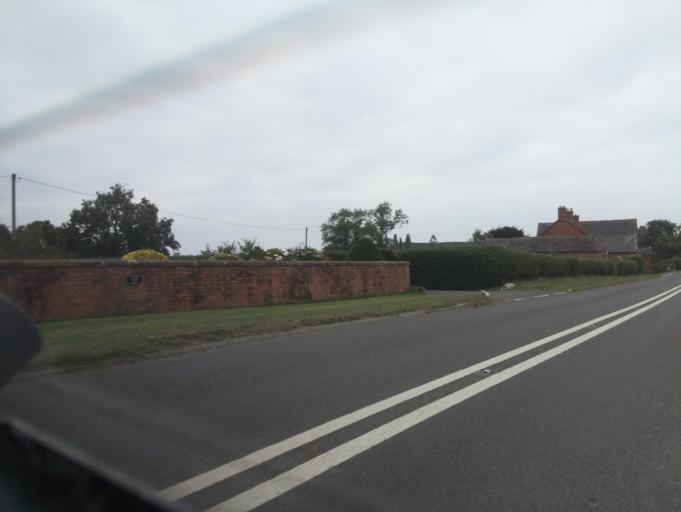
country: GB
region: England
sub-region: Shropshire
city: Shawbury
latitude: 52.7980
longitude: -2.6299
